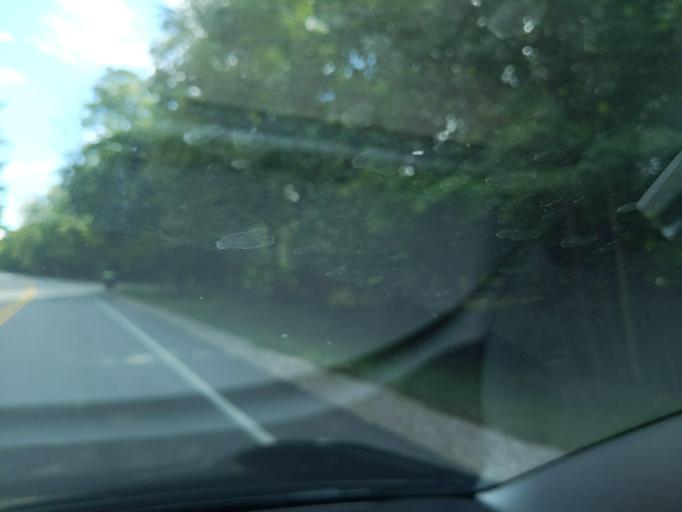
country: US
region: Michigan
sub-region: Antrim County
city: Bellaire
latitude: 45.0360
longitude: -85.2968
